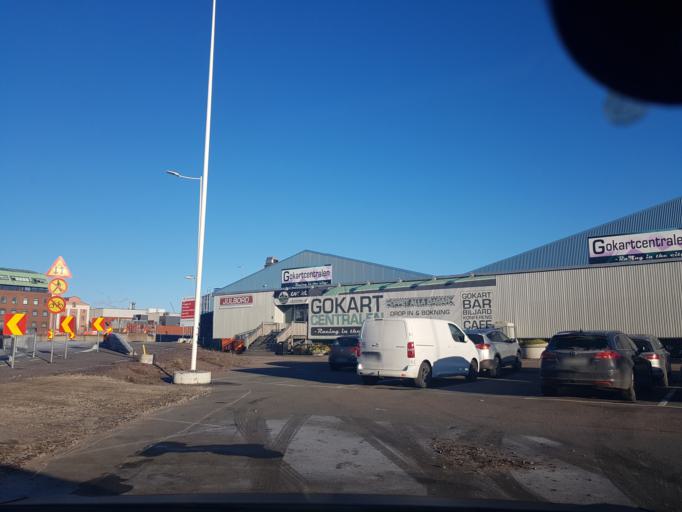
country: SE
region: Vaestra Goetaland
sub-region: Goteborg
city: Goeteborg
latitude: 57.7127
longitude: 11.9755
